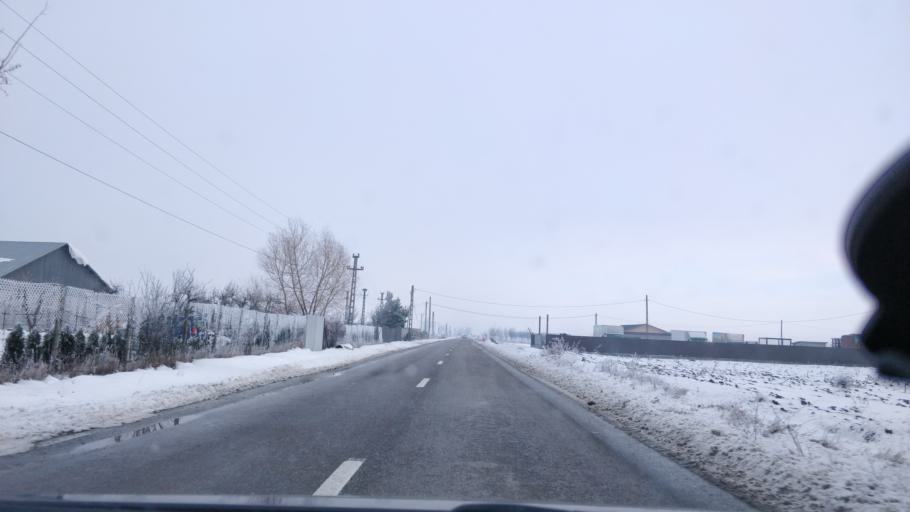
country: RO
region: Vrancea
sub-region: Comuna Vrancioaia
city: Focsani
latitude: 45.6978
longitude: 27.2181
